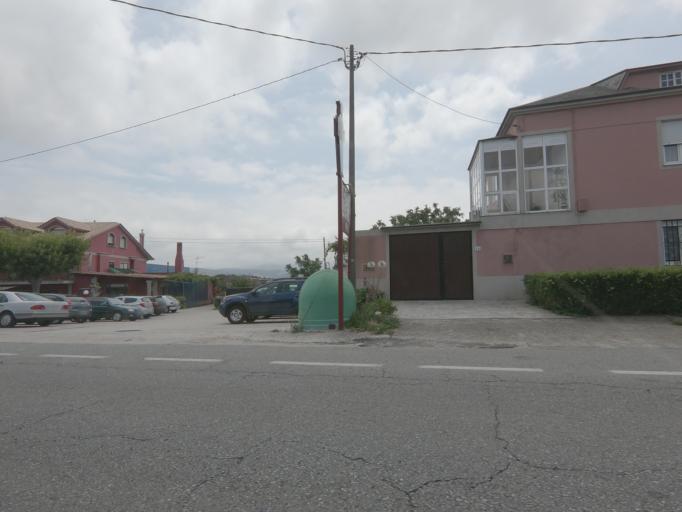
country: ES
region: Galicia
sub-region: Provincia de Pontevedra
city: A Guarda
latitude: 41.9109
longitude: -8.8536
